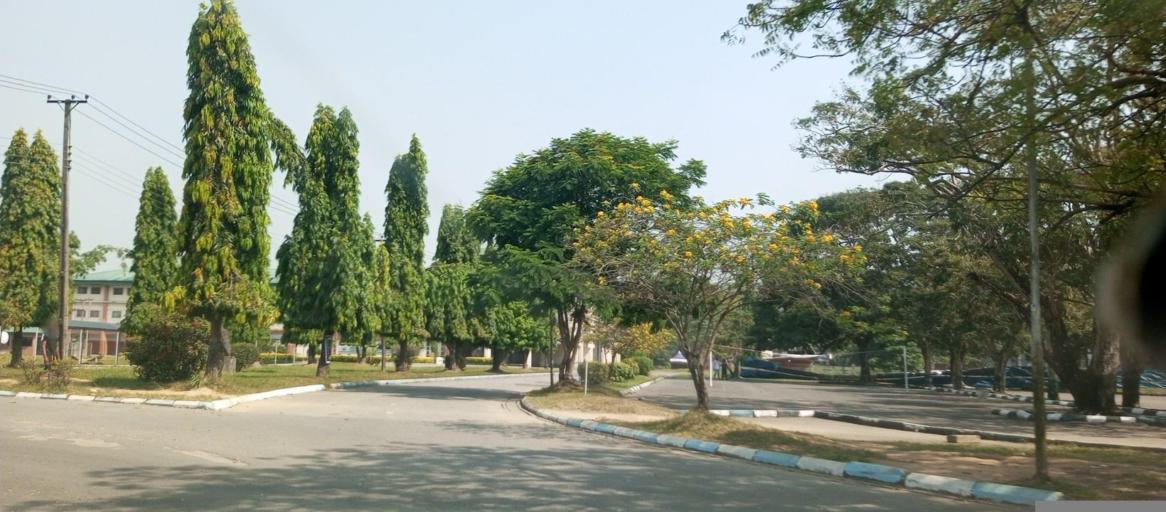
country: NG
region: Rivers
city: Emuoha
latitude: 4.9026
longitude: 6.9207
